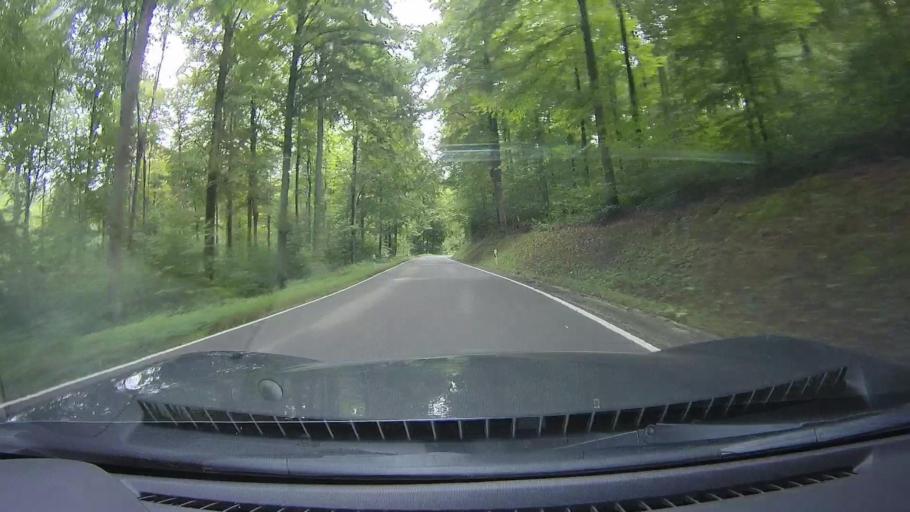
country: DE
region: Baden-Wuerttemberg
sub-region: Regierungsbezirk Stuttgart
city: Lowenstein
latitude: 49.0452
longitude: 9.3882
